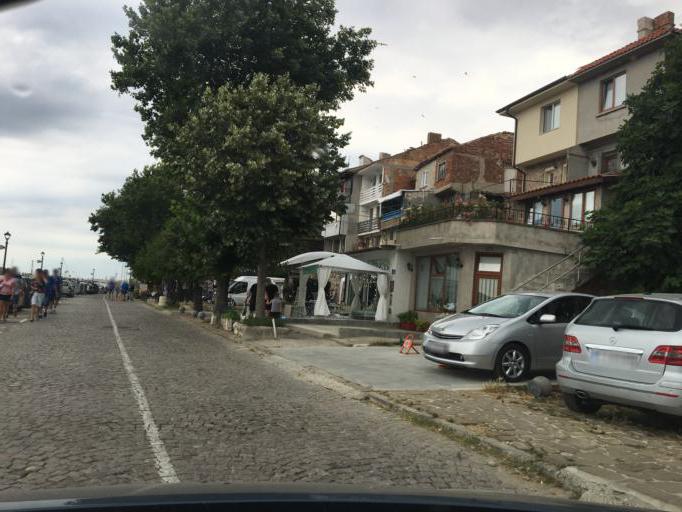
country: BG
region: Burgas
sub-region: Obshtina Sozopol
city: Sozopol
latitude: 42.4228
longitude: 27.6924
